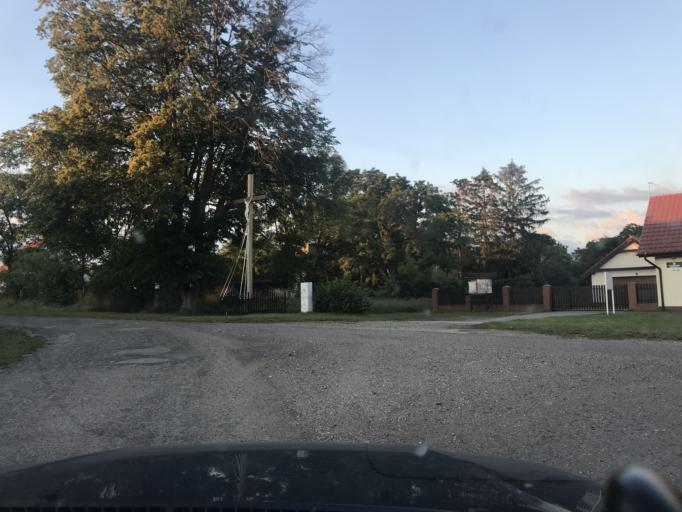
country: PL
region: West Pomeranian Voivodeship
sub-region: Powiat stargardzki
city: Chociwel
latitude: 53.4674
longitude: 15.3788
